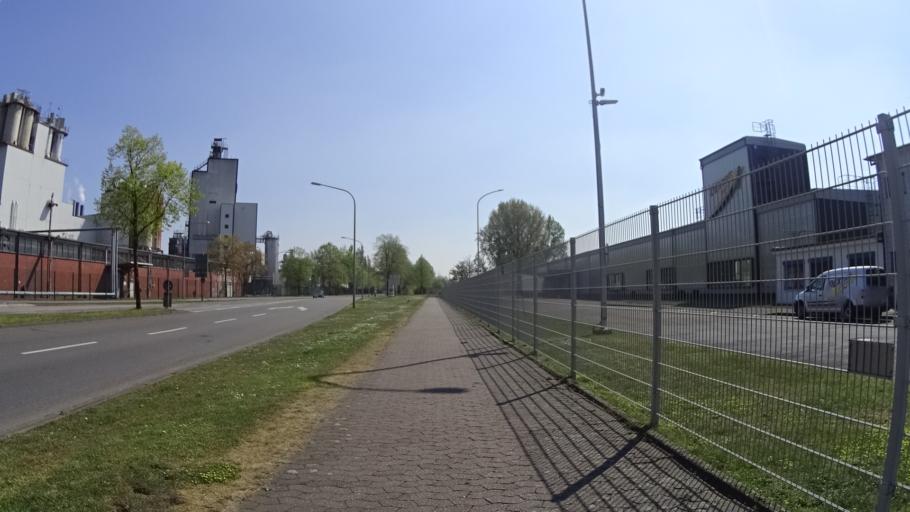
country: DE
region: North Rhine-Westphalia
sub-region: Regierungsbezirk Dusseldorf
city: Krefeld
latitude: 51.3413
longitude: 6.6600
